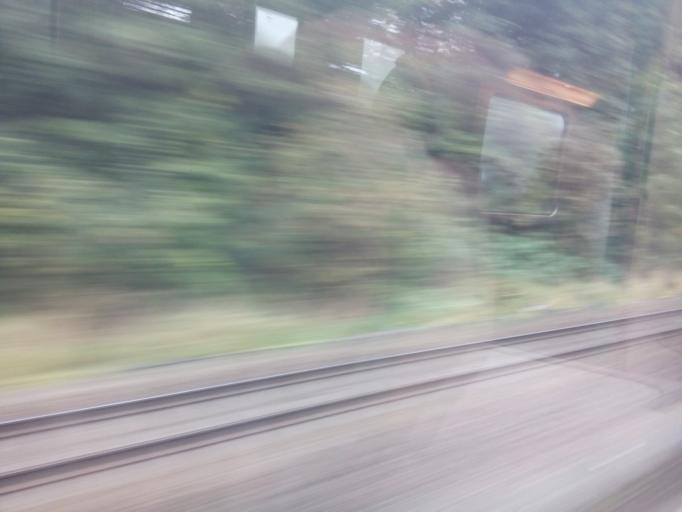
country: GB
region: England
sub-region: Kirklees
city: Mirfield
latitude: 53.6725
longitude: -1.6660
